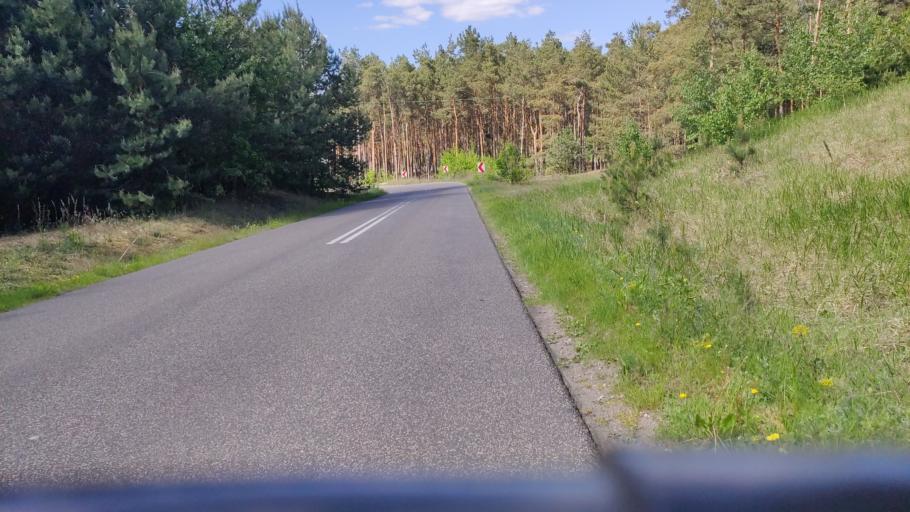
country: PL
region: Kujawsko-Pomorskie
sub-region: Wloclawek
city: Wloclawek
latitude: 52.5892
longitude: 19.0935
